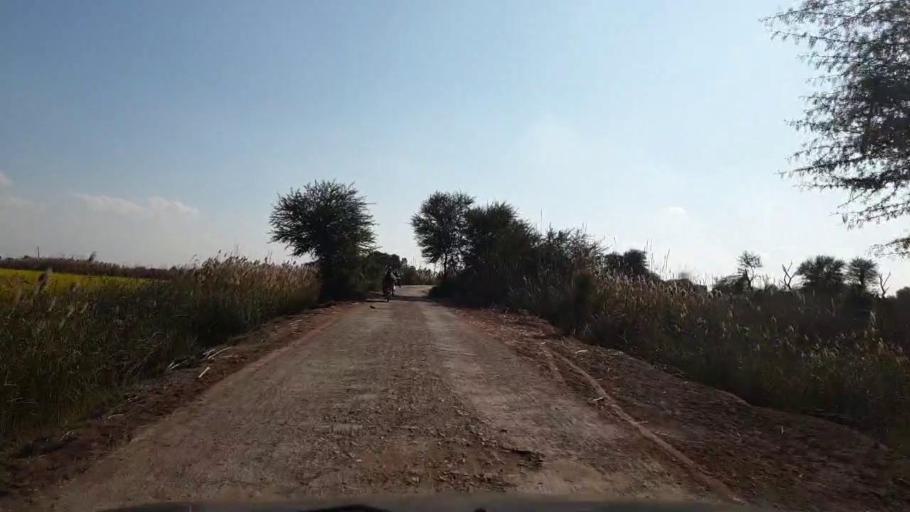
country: PK
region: Sindh
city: Sinjhoro
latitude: 25.9775
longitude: 68.7252
